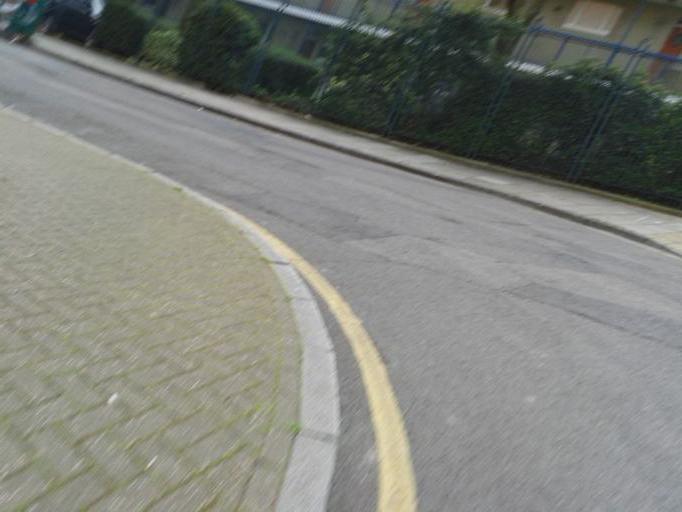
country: GB
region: England
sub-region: Greater London
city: Clerkenwell
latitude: 51.5274
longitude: -0.1226
